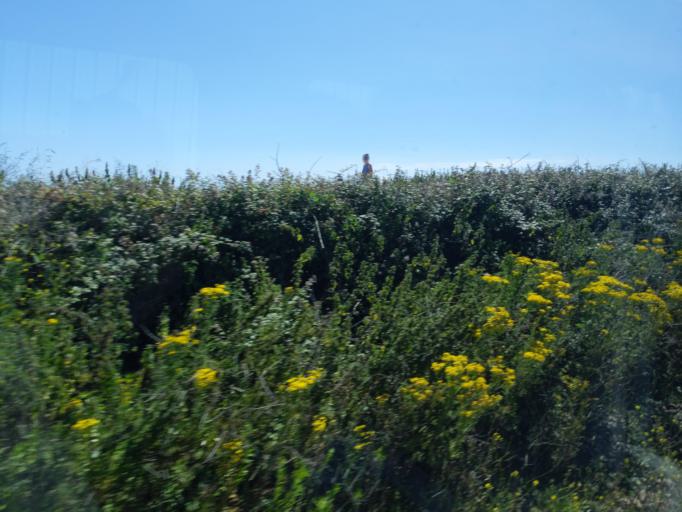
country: GB
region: England
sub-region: Cornwall
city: Penzance
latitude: 50.1278
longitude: -5.5100
